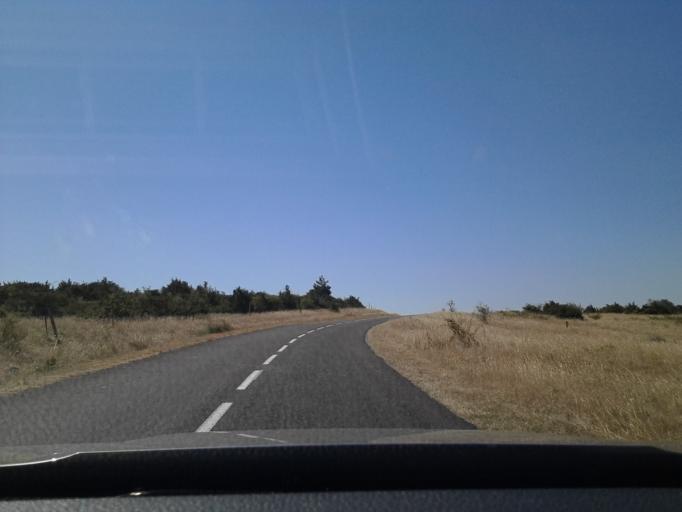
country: FR
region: Languedoc-Roussillon
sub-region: Departement de l'Herault
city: Montpeyroux
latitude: 43.7675
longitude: 3.4664
